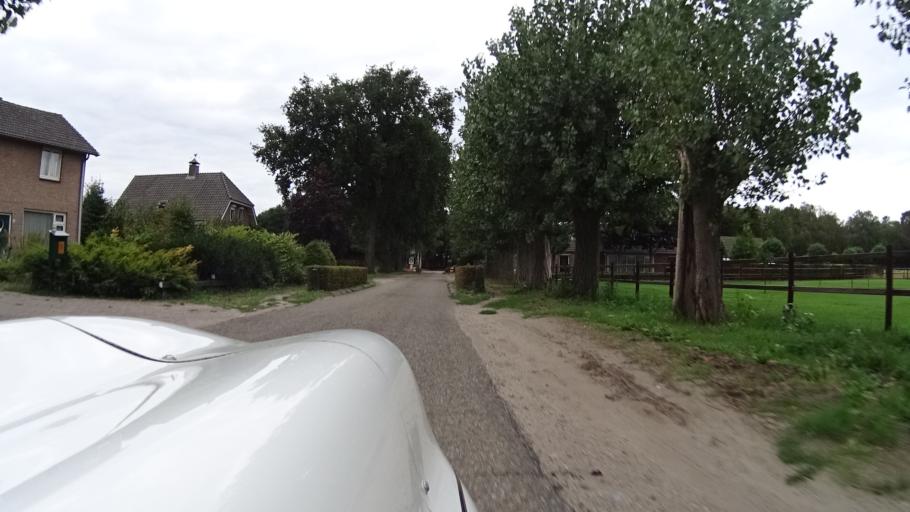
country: NL
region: North Brabant
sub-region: Gemeente Veghel
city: Mariaheide
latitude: 51.6592
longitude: 5.5619
